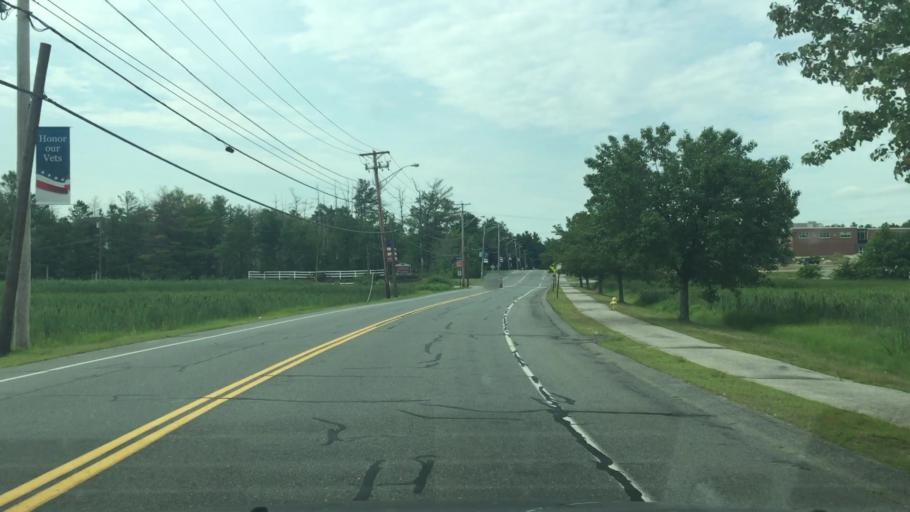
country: US
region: New Hampshire
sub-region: Rockingham County
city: Salem
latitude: 42.7833
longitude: -71.2098
